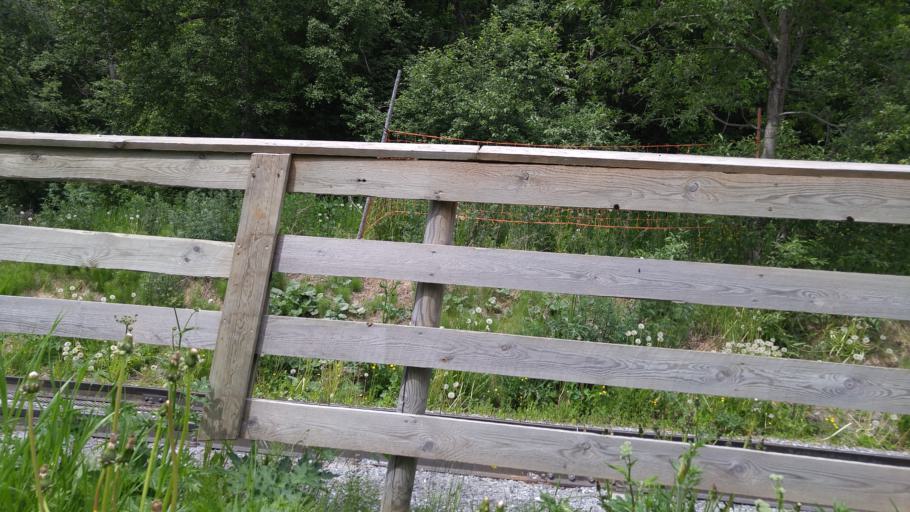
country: SE
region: Jaemtland
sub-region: Are Kommun
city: Are
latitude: 63.4015
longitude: 13.0818
